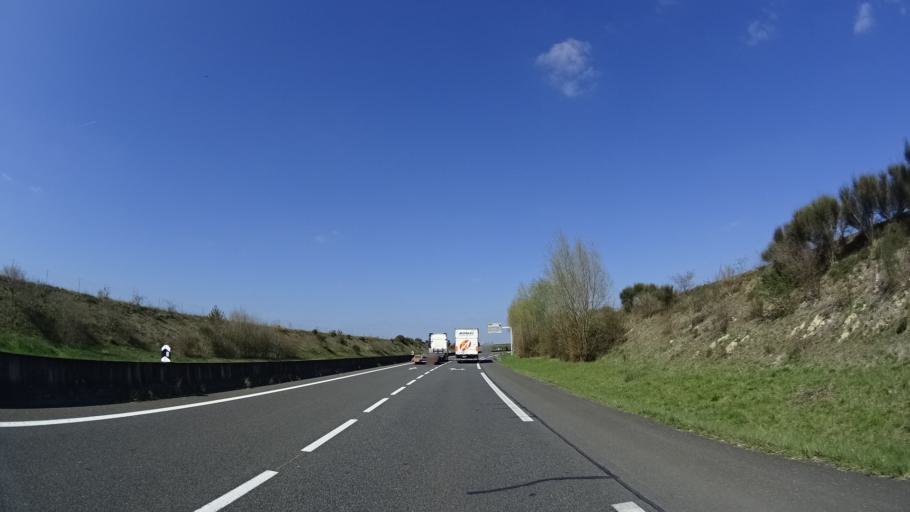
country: FR
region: Pays de la Loire
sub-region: Departement de Maine-et-Loire
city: Saint-Jean
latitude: 47.2526
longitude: -0.3304
